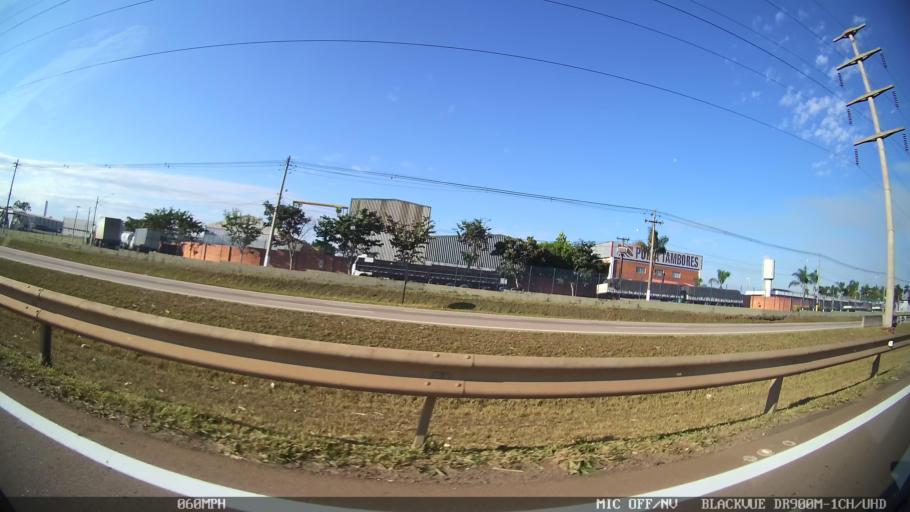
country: BR
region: Sao Paulo
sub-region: Piracicaba
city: Piracicaba
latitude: -22.6656
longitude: -47.6067
